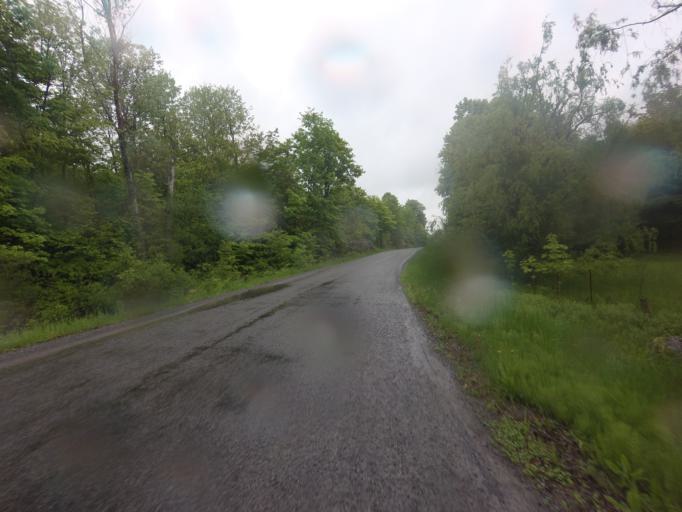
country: CA
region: Ontario
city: Gananoque
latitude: 44.5412
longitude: -76.3708
